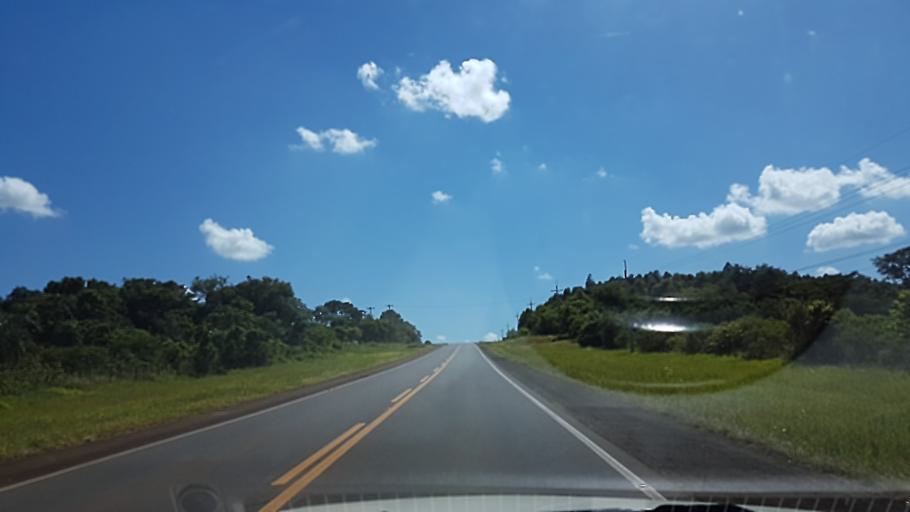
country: PY
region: Itapua
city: Carmen del Parana
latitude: -27.2182
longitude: -56.0968
